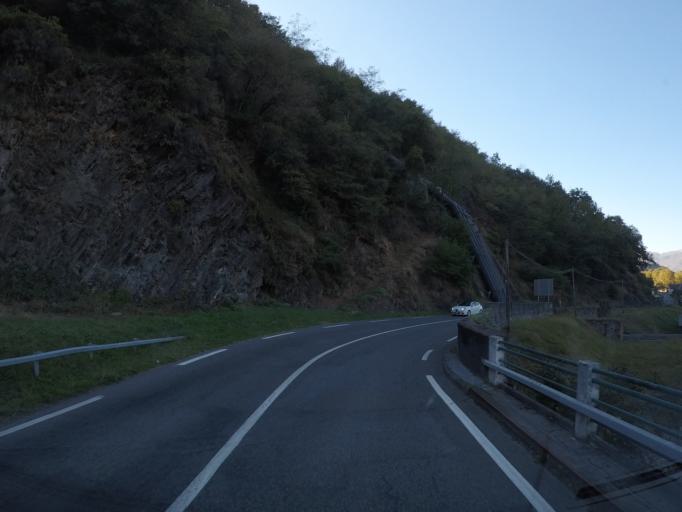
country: FR
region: Midi-Pyrenees
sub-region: Departement des Hautes-Pyrenees
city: Pierrefitte-Nestalas
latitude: 42.9515
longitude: -0.0694
